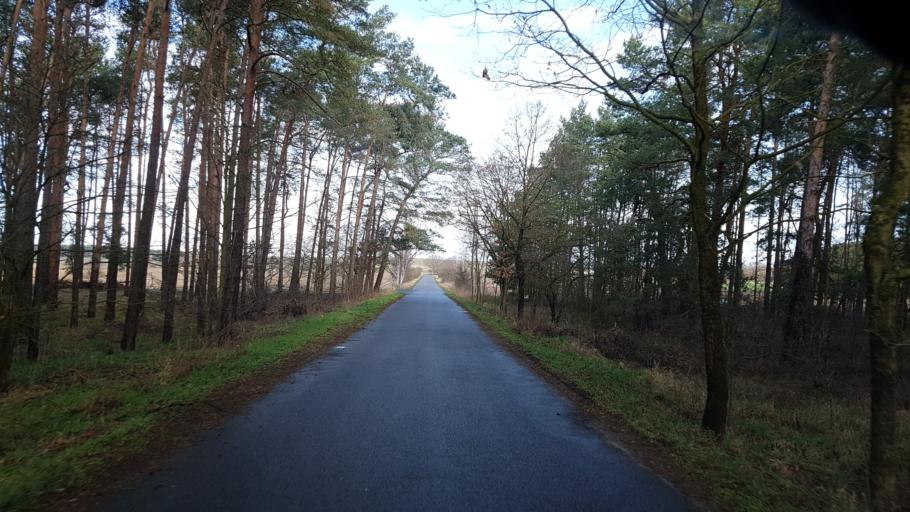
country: DE
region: Brandenburg
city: Schlieben
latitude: 51.7141
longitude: 13.3143
